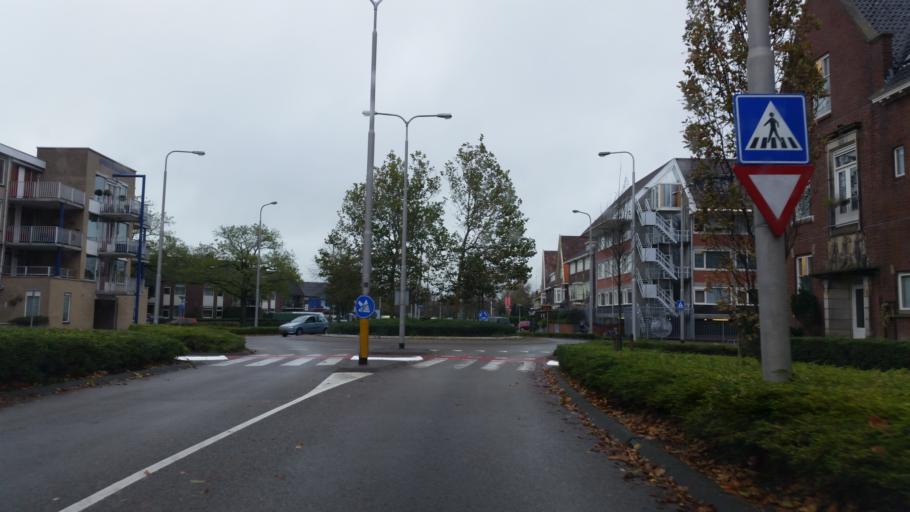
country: NL
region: Friesland
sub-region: Gemeente Leeuwarden
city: Leeuwarden
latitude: 53.2070
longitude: 5.8024
